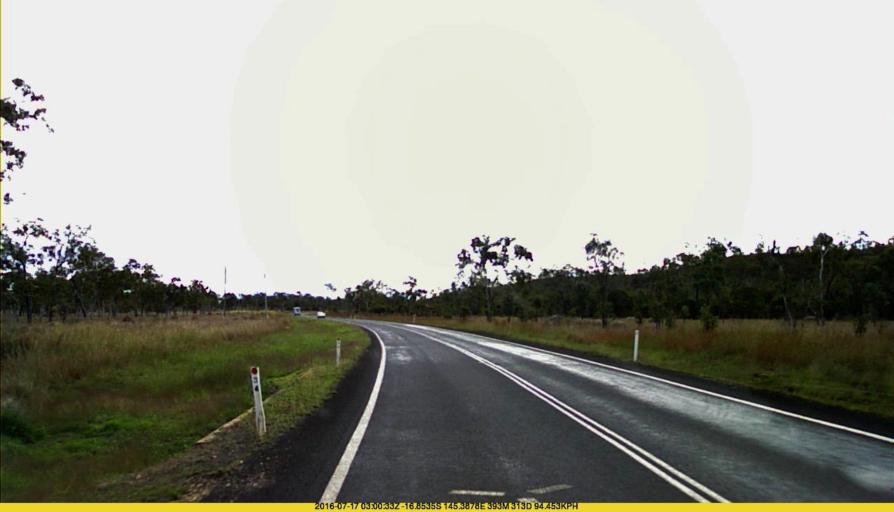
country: AU
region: Queensland
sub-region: Tablelands
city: Mareeba
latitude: -16.8597
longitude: 145.3928
